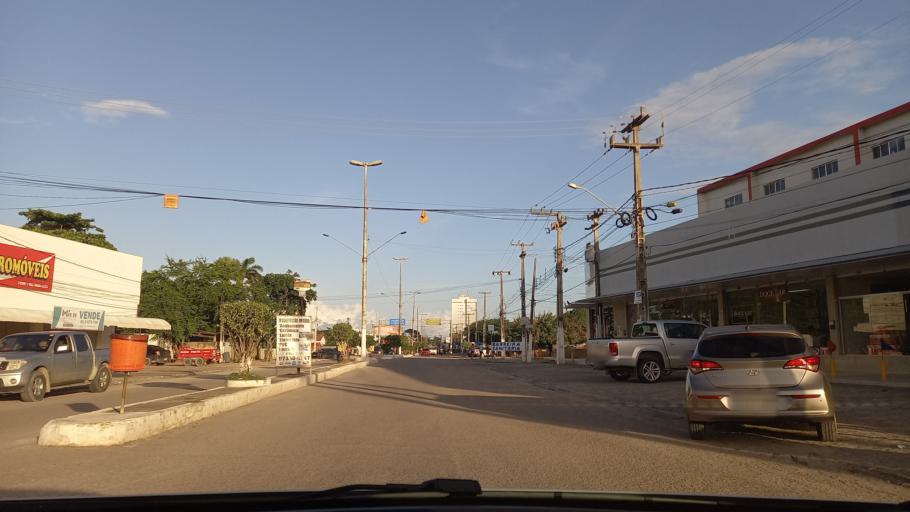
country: BR
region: Pernambuco
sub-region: Sao Jose Da Coroa Grande
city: Sao Jose da Coroa Grande
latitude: -8.8947
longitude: -35.1499
